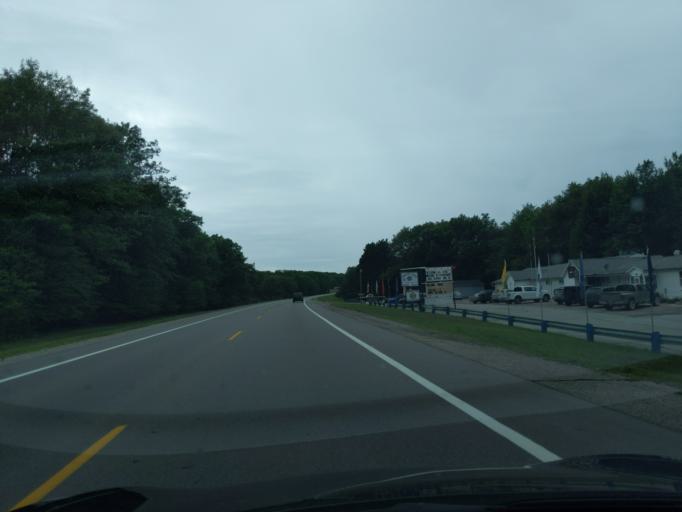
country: US
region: Michigan
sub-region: Clare County
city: Harrison
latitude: 44.0182
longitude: -84.8197
